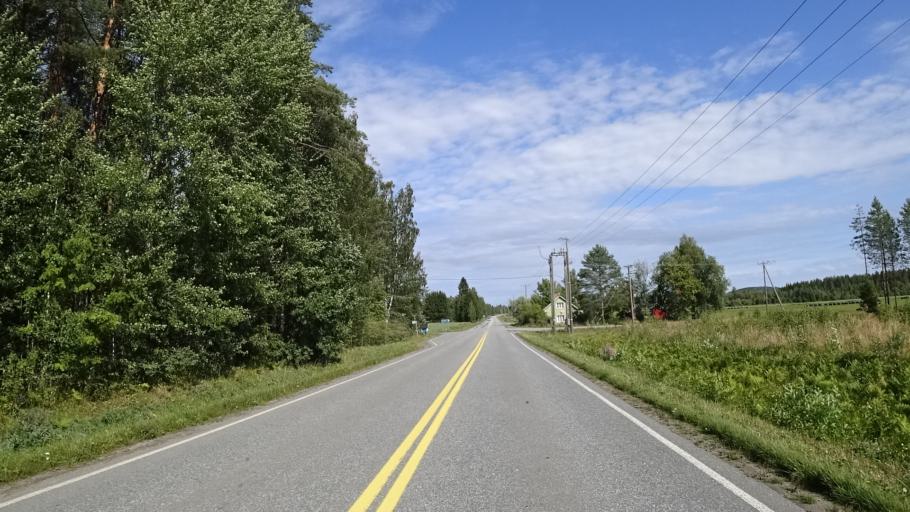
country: FI
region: North Karelia
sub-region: Joensuu
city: Pyhaeselkae
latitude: 62.3695
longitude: 29.8405
